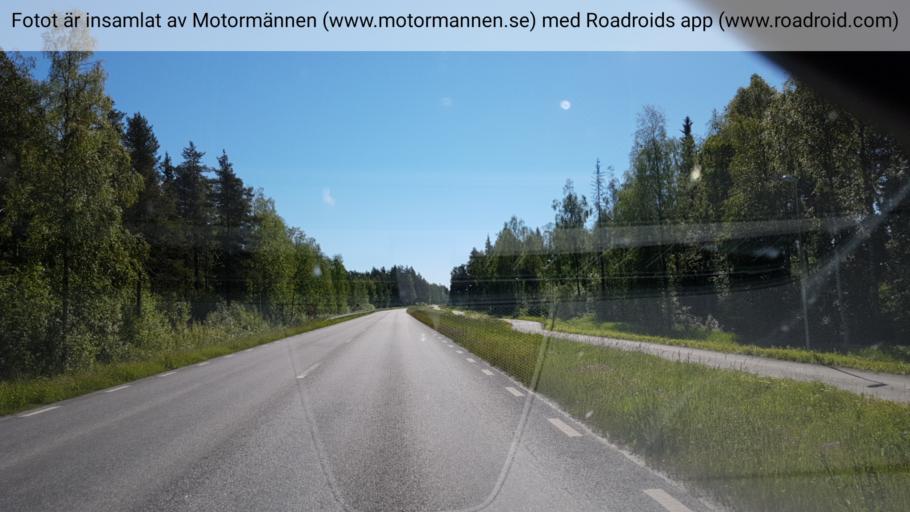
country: SE
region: Norrbotten
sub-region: Bodens Kommun
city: Boden
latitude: 65.8286
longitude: 21.6422
